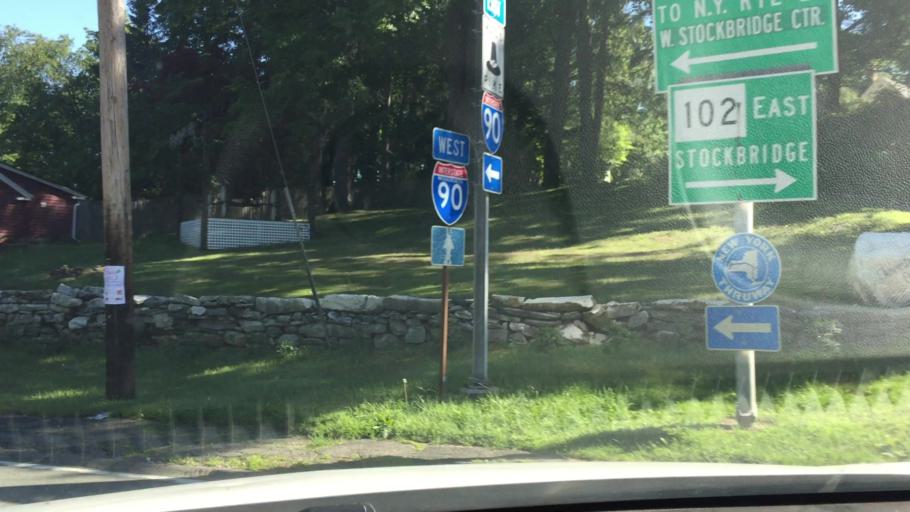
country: US
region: Massachusetts
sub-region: Berkshire County
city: West Stockbridge
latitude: 42.3302
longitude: -73.3648
